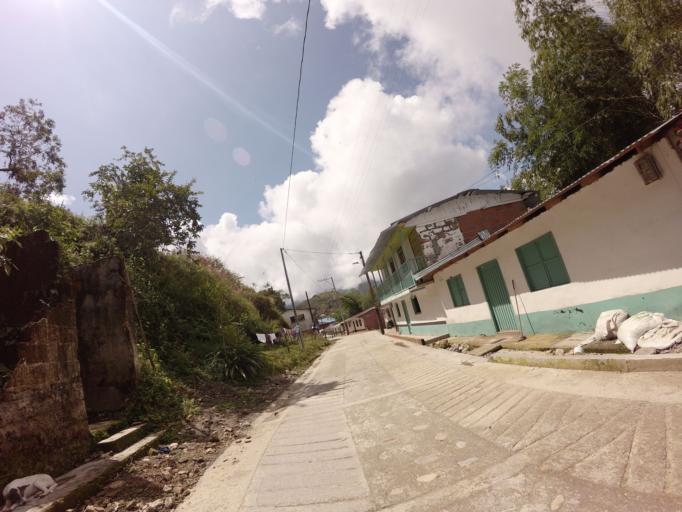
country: CO
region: Antioquia
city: Narino
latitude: 5.5015
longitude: -75.1824
